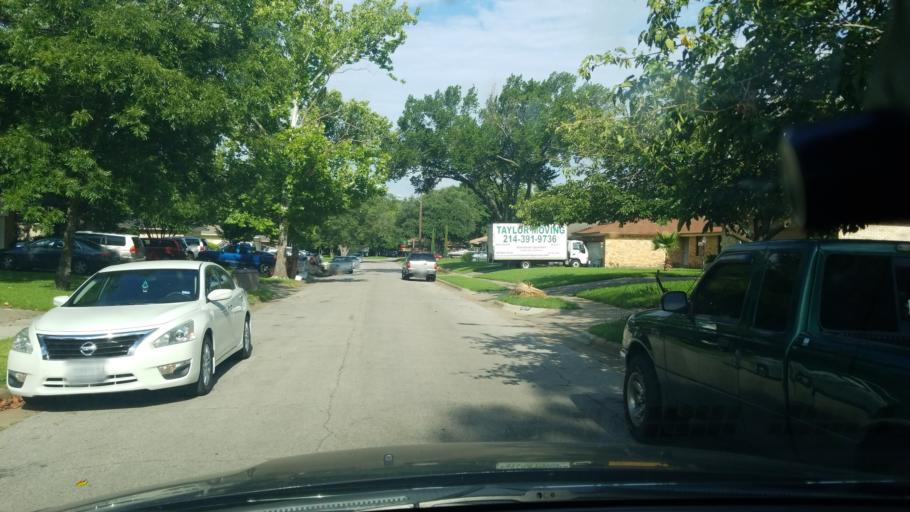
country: US
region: Texas
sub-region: Dallas County
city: Balch Springs
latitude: 32.7428
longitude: -96.6675
